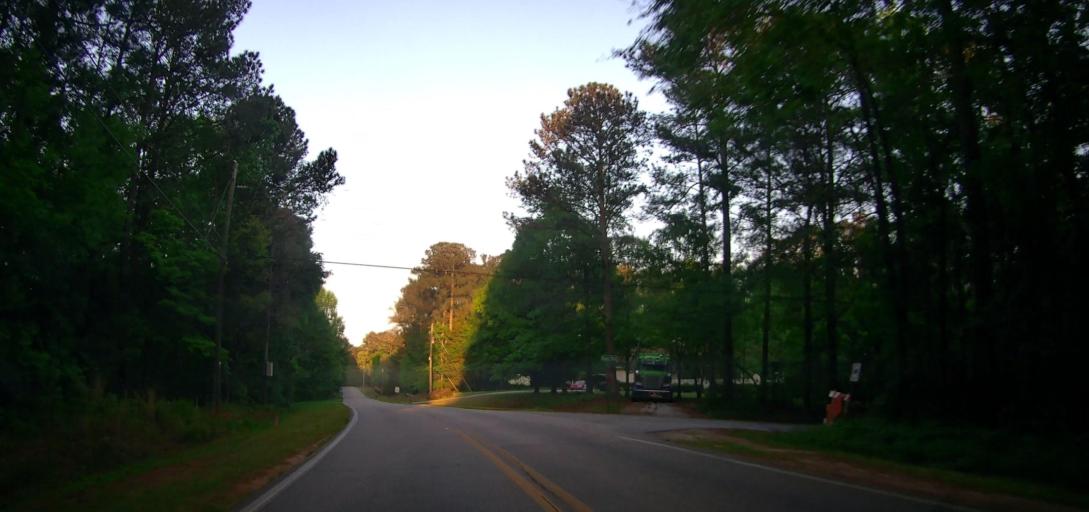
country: US
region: Georgia
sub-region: Henry County
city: McDonough
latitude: 33.4061
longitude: -84.1048
